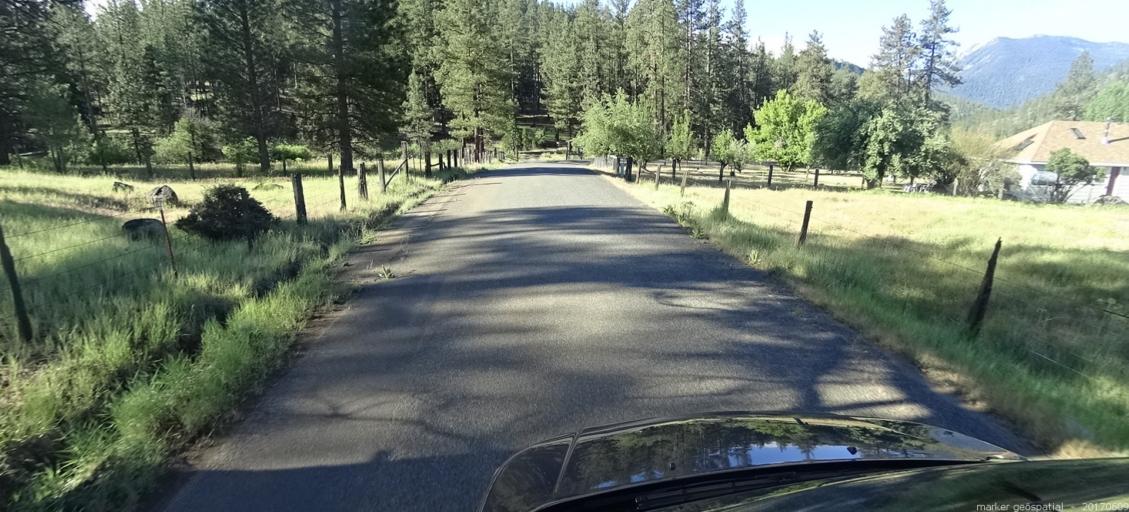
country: US
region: California
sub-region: Siskiyou County
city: Weed
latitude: 41.3261
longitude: -122.7188
